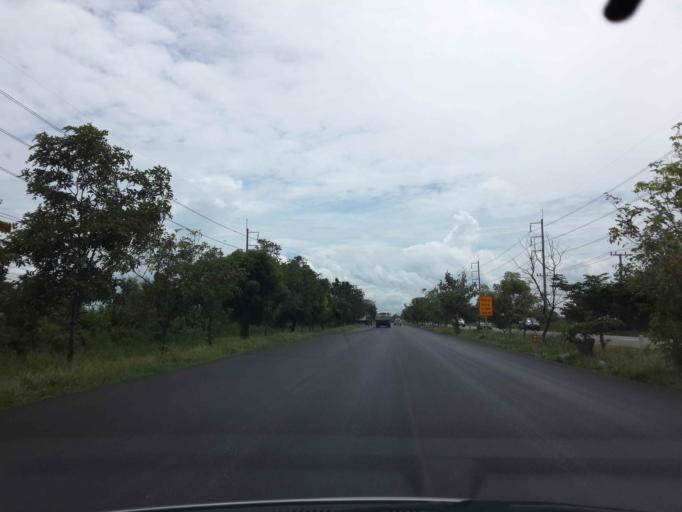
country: TH
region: Ratchaburi
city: Pak Tho
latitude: 13.4237
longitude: 99.8083
